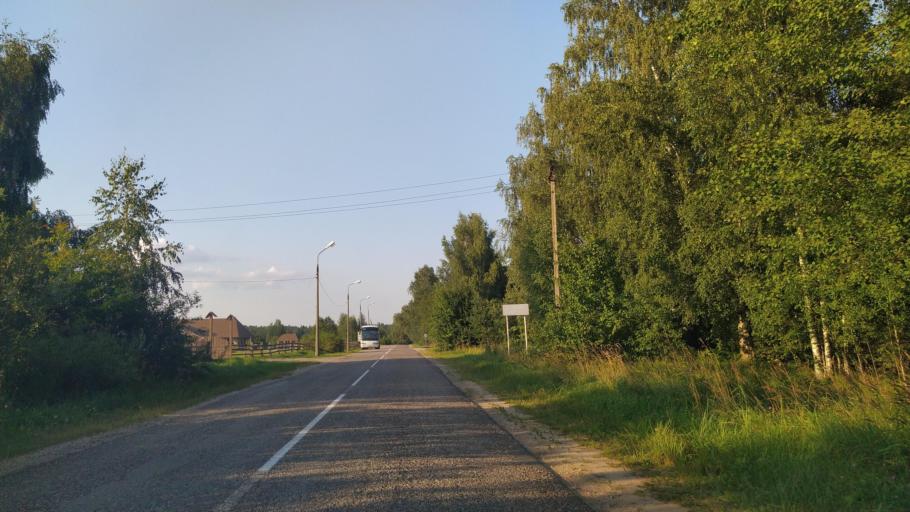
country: RU
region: Pskov
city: Pushkinskiye Gory
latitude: 57.0403
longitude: 28.9134
